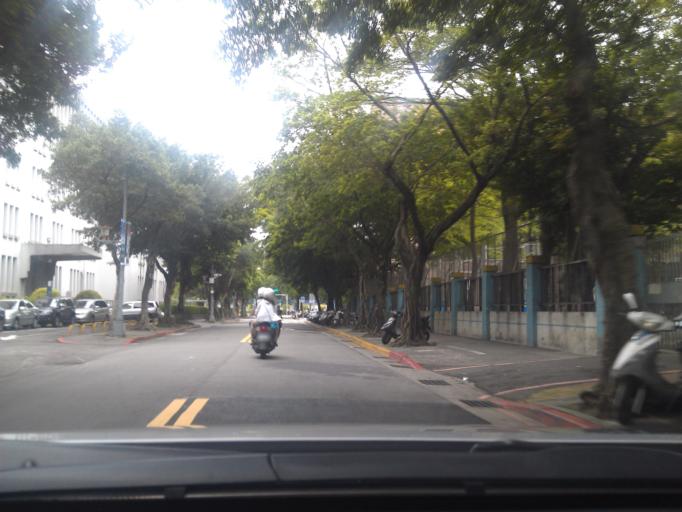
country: TW
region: Taipei
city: Taipei
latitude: 25.0386
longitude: 121.5156
